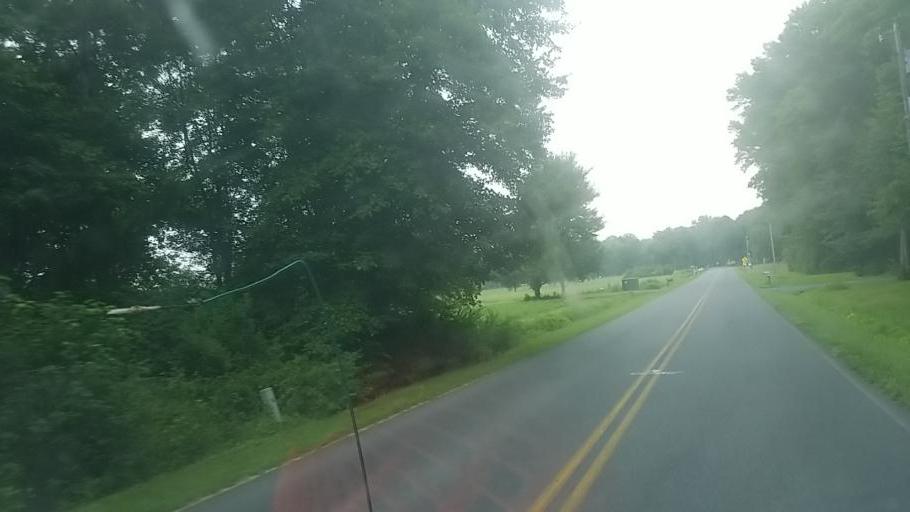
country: US
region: Maryland
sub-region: Wicomico County
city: Delmar
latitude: 38.4134
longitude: -75.5142
